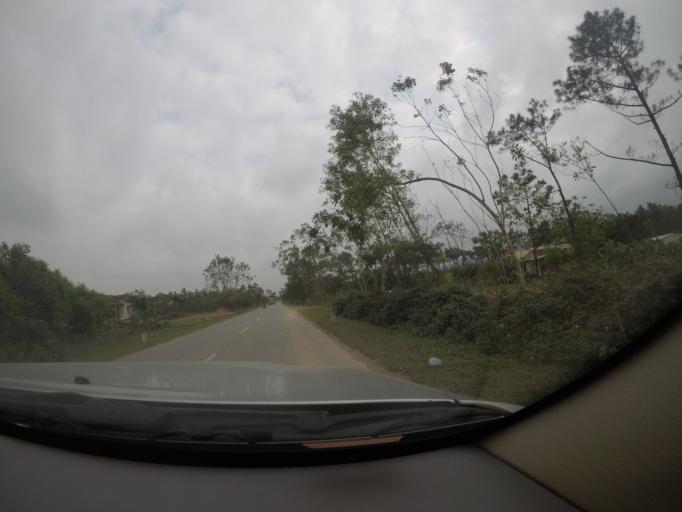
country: VN
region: Quang Binh
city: Quan Hau
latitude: 17.4079
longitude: 106.6031
